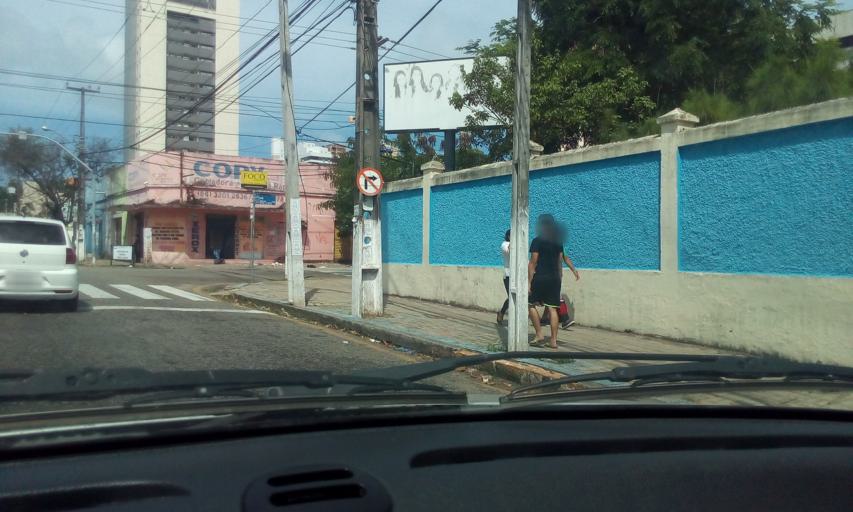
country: BR
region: Rio Grande do Norte
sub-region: Natal
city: Natal
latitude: -5.7901
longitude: -35.2052
